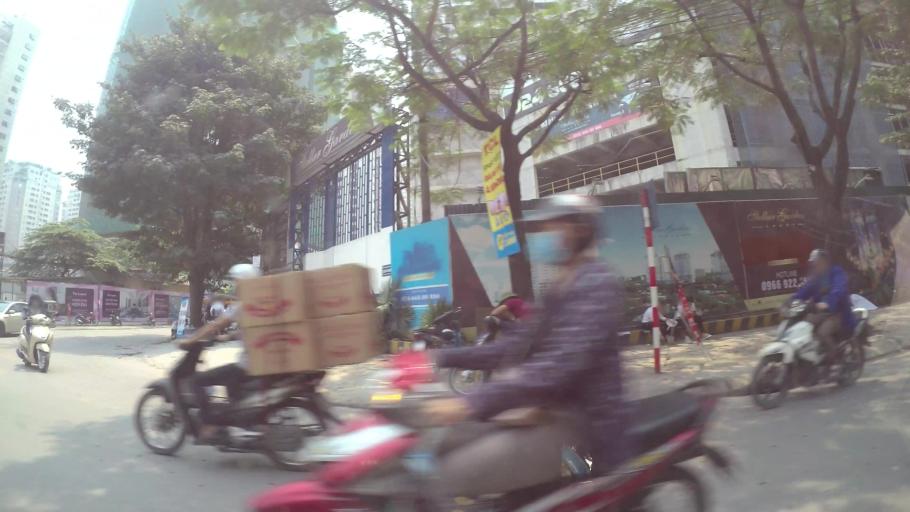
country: VN
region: Ha Noi
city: Thanh Xuan
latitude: 21.0010
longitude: 105.8035
